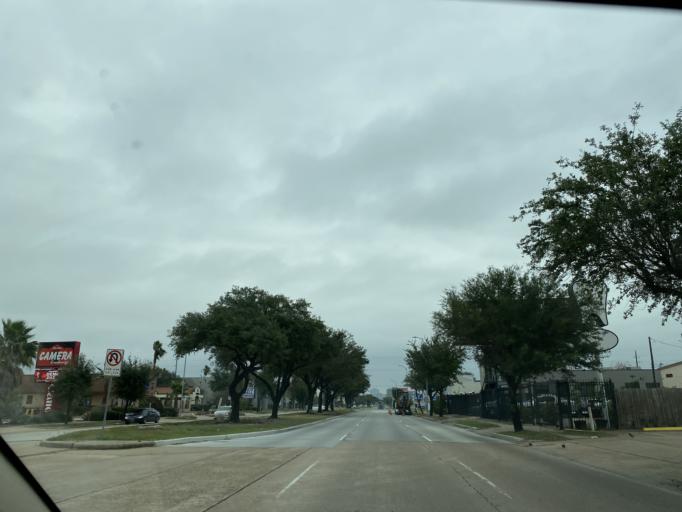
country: US
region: Texas
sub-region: Harris County
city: Bellaire
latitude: 29.7315
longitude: -95.4830
